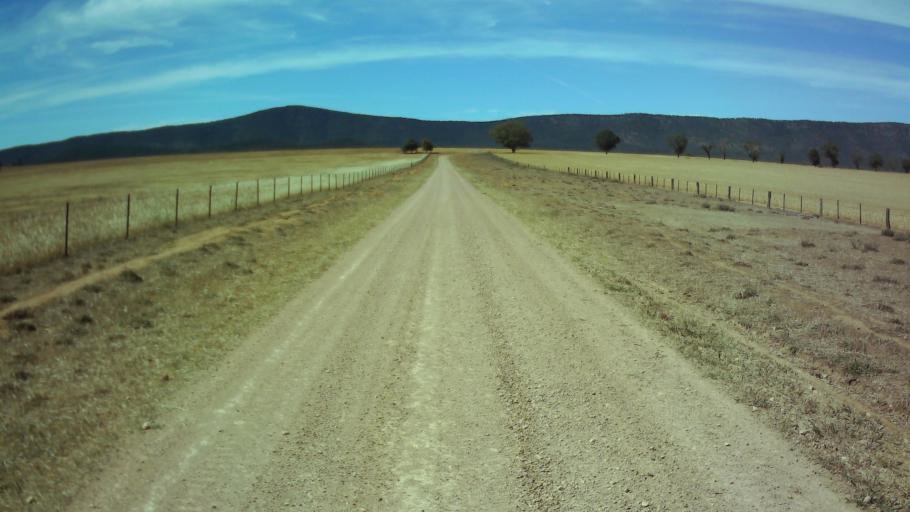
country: AU
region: New South Wales
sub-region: Weddin
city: Grenfell
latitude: -33.9466
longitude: 148.0667
